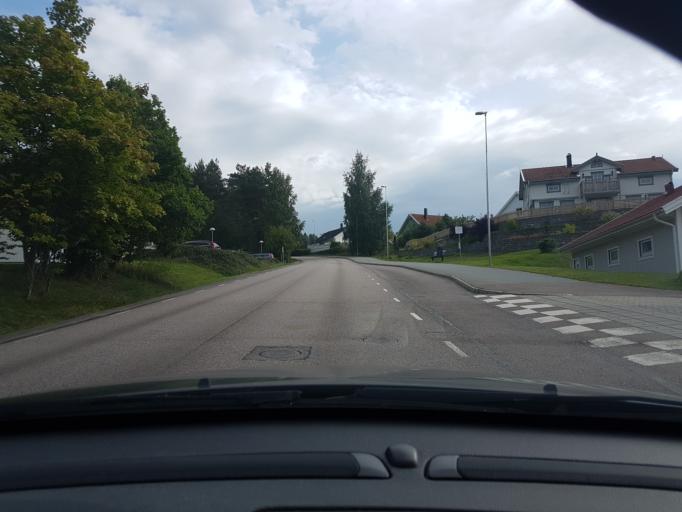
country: SE
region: Vaestra Goetaland
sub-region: Ale Kommun
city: Surte
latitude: 57.8518
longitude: 12.0315
